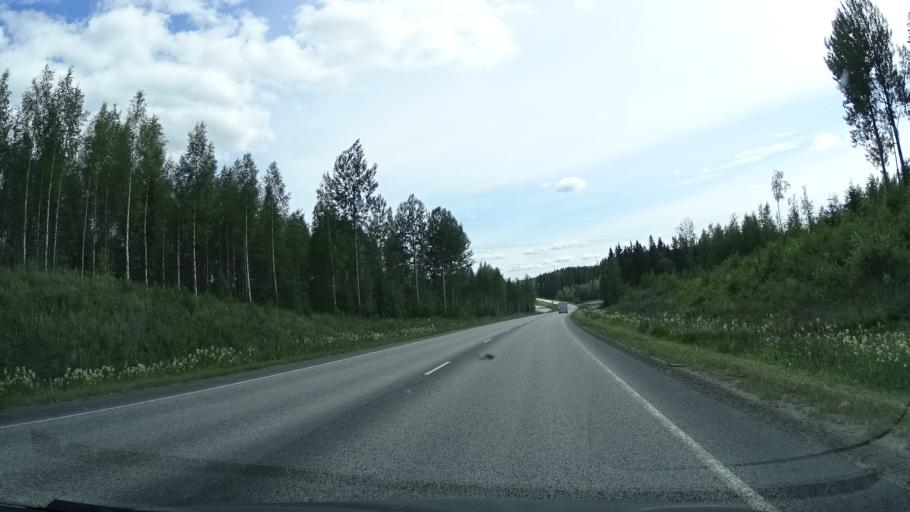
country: FI
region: Central Finland
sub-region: Jyvaeskylae
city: Jyvaeskylae
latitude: 62.2593
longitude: 25.6063
